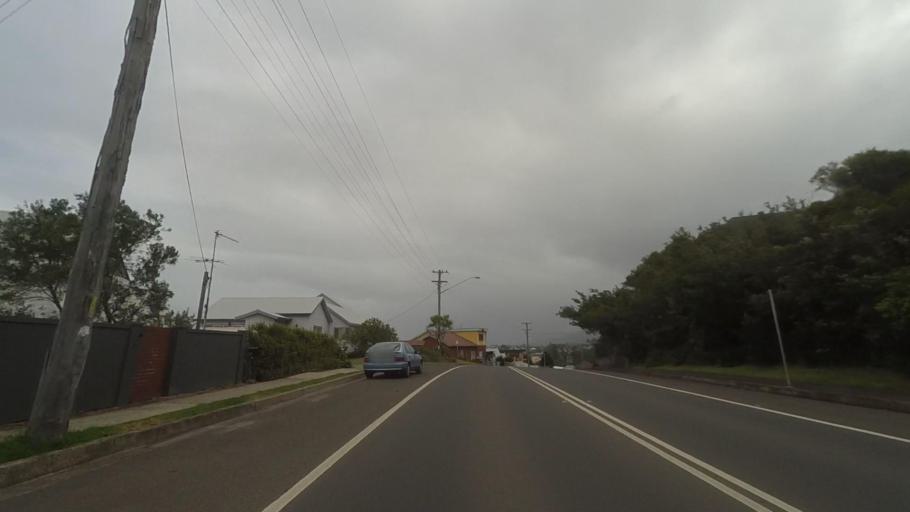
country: AU
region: New South Wales
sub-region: Wollongong
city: Bulli
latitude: -34.3105
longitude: 150.9321
